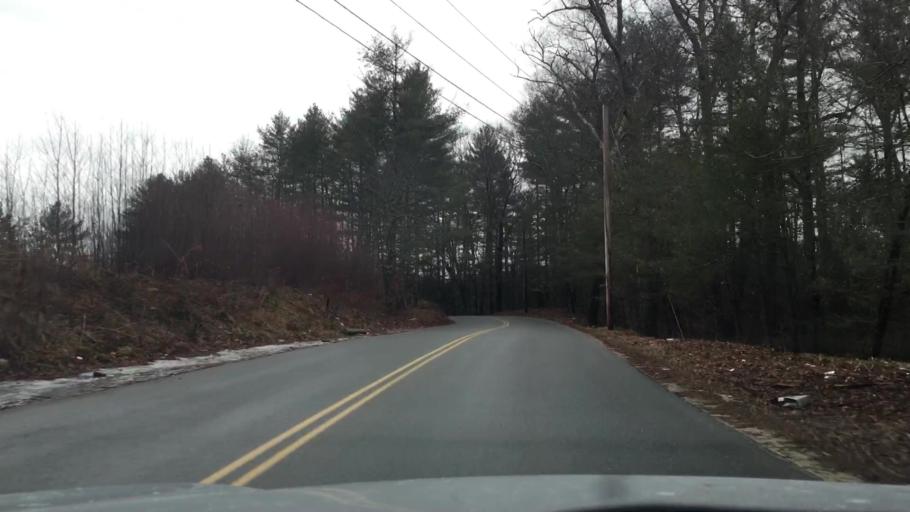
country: US
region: Massachusetts
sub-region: Worcester County
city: Athol
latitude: 42.5746
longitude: -72.2557
